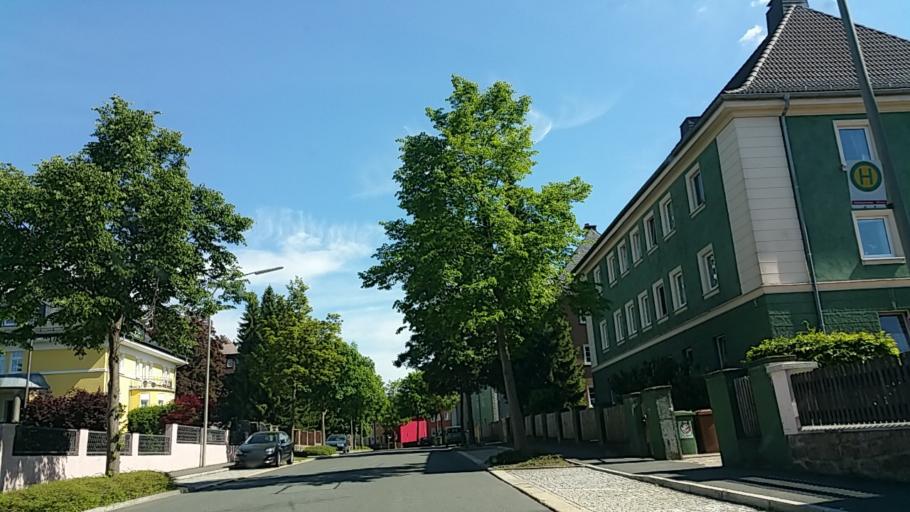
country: DE
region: Bavaria
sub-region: Upper Franconia
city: Schwarzenbach an der Saale
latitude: 50.2188
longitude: 11.9437
